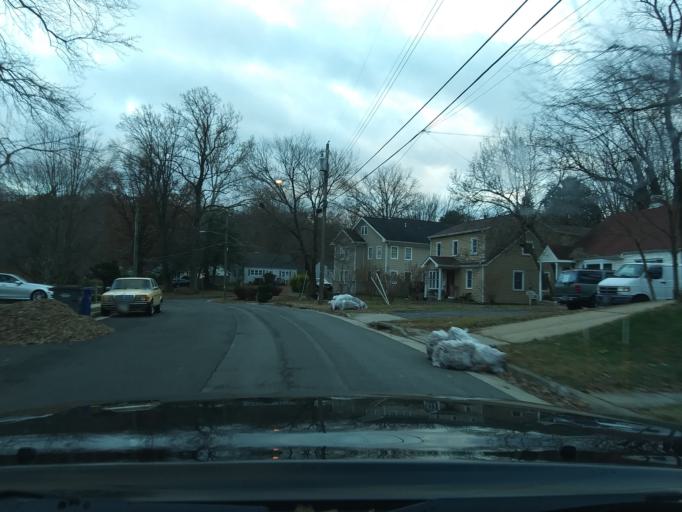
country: US
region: Virginia
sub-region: Fairfax County
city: Jefferson
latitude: 38.8619
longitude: -77.1757
